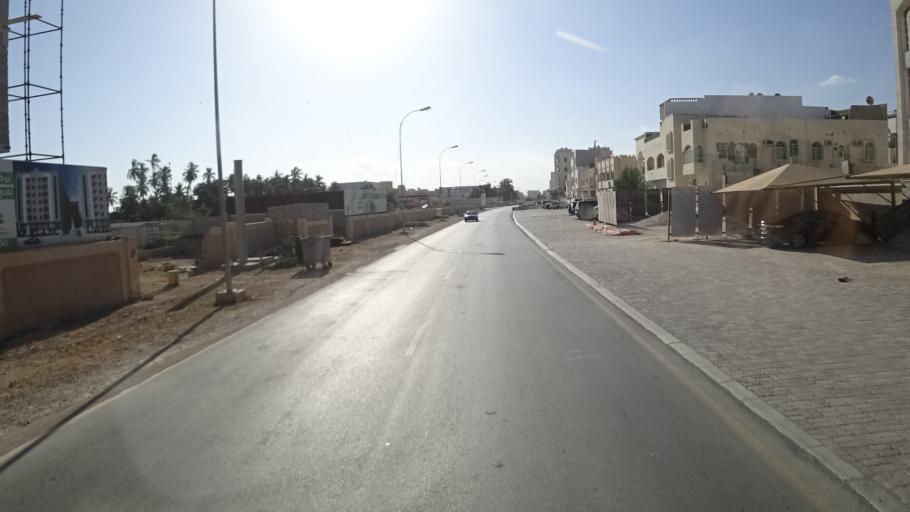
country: OM
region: Zufar
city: Salalah
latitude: 17.0055
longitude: 54.0737
